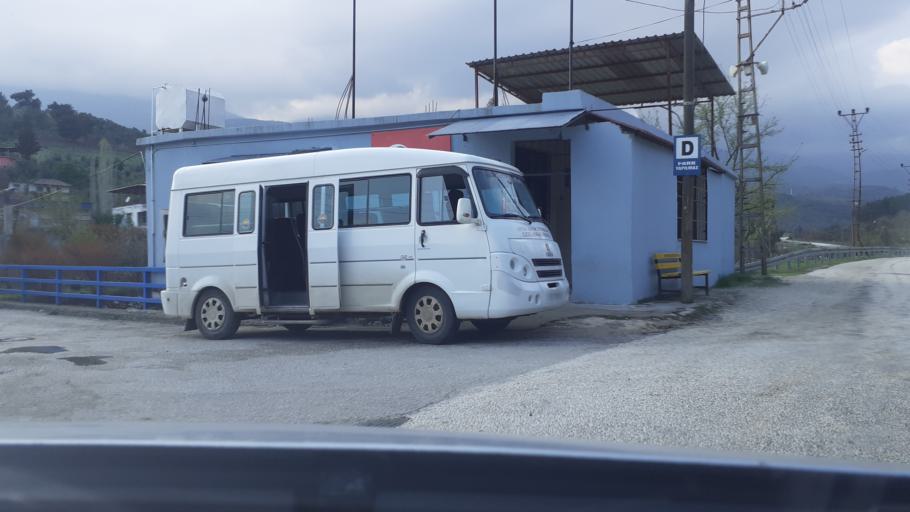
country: TR
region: Hatay
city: Kirikhan
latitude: 36.5060
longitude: 36.3228
